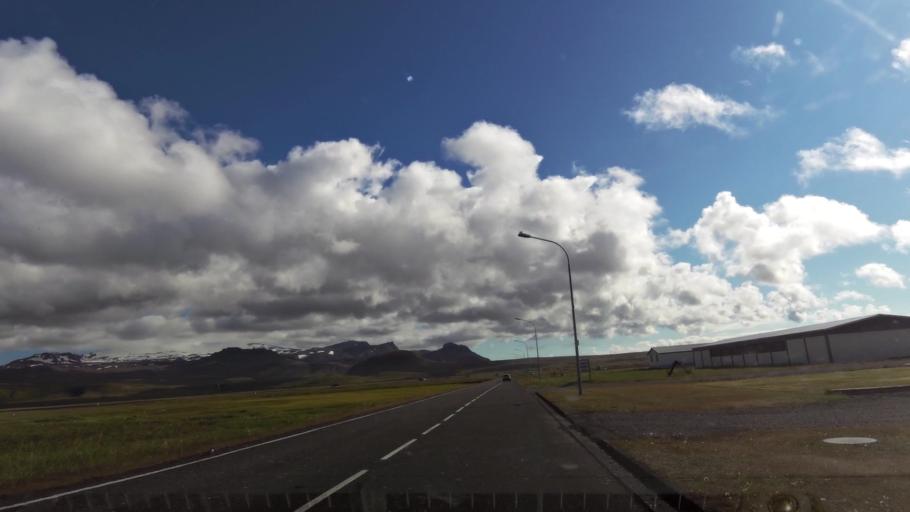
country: IS
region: West
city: Olafsvik
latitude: 64.9220
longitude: -23.8174
